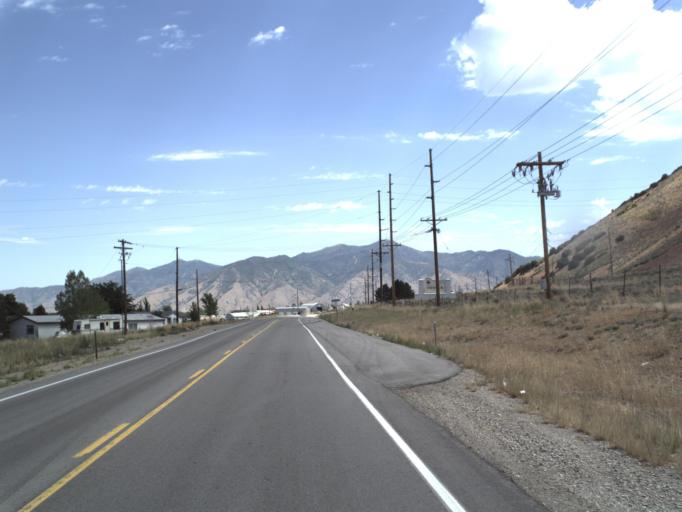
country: US
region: Utah
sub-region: Tooele County
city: Tooele
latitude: 40.5038
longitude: -112.3211
